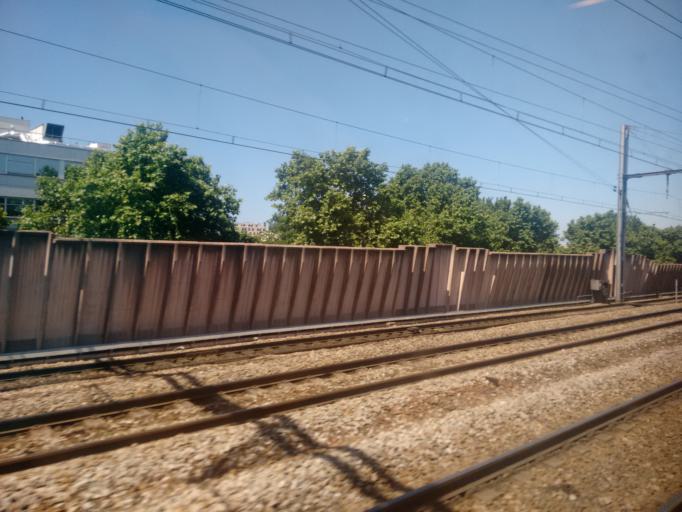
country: FR
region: Ile-de-France
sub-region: Departement des Hauts-de-Seine
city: Malakoff
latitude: 48.8138
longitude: 2.2983
